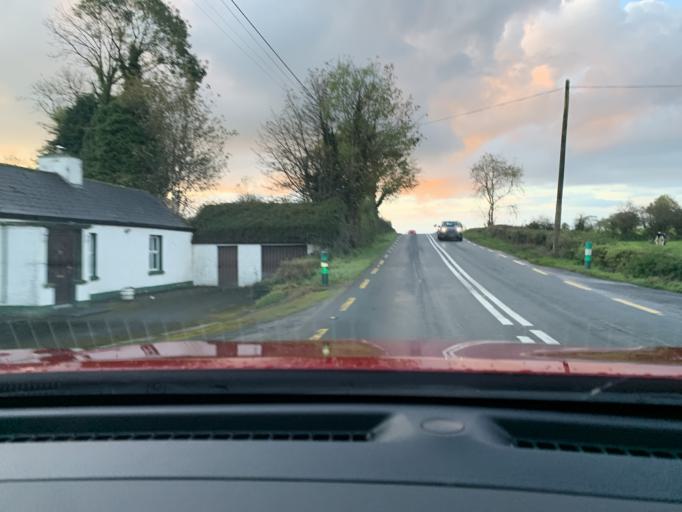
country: IE
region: Connaught
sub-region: Sligo
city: Ballymote
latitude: 54.1158
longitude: -8.4255
